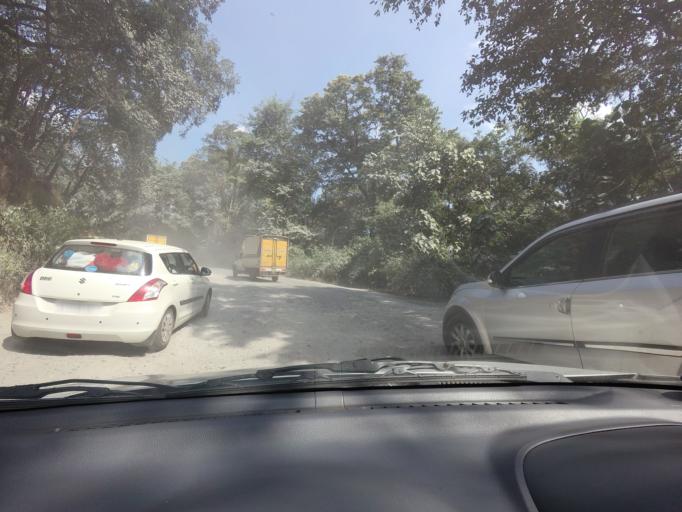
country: IN
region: Karnataka
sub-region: Hassan
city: Sakleshpur
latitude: 12.8272
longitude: 75.5857
